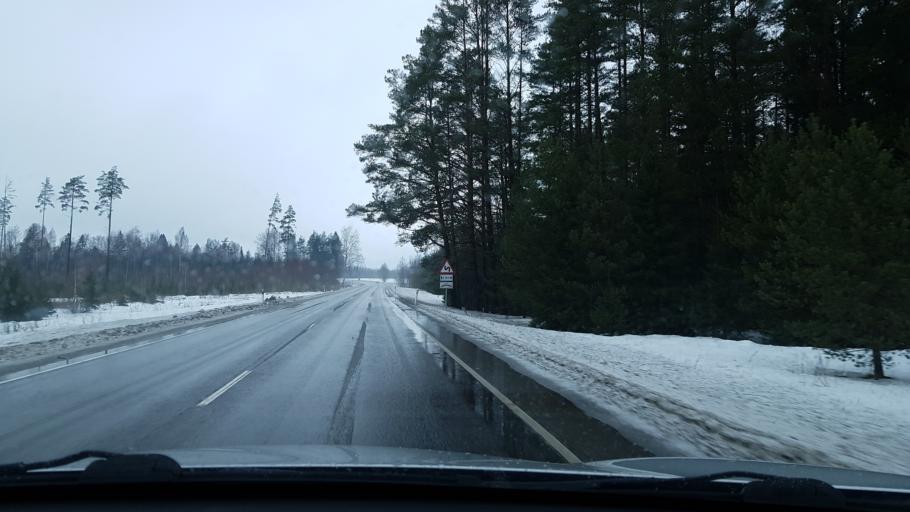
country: EE
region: Raplamaa
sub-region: Kehtna vald
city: Kehtna
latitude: 58.8975
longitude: 24.9031
